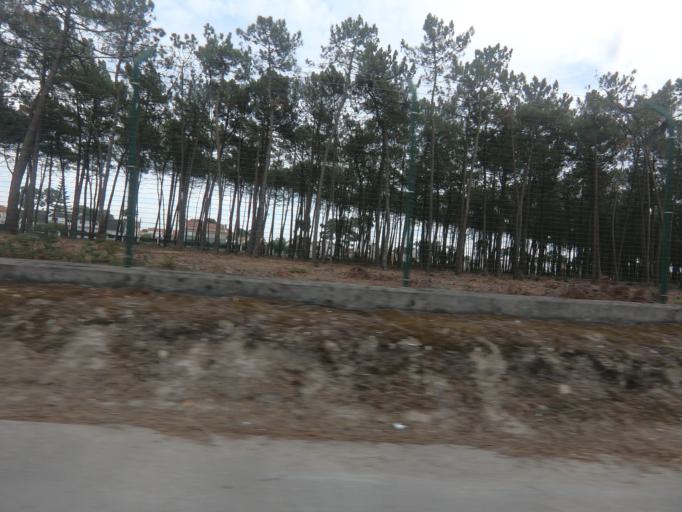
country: PT
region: Setubal
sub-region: Almada
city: Charneca
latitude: 38.5954
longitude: -9.1882
